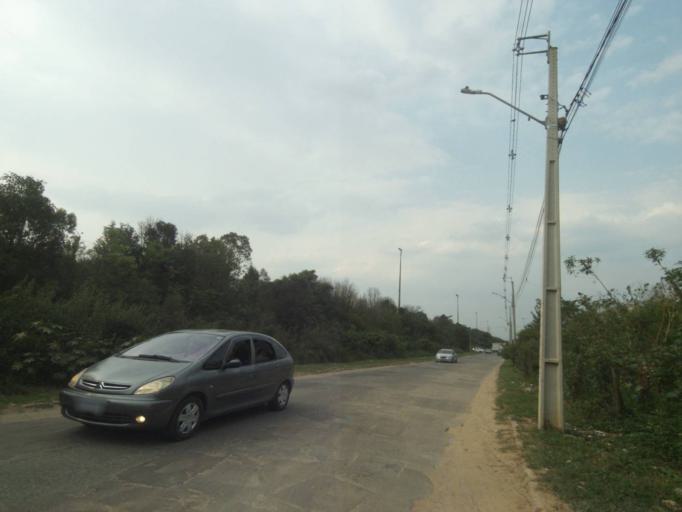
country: BR
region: Parana
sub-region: Sao Jose Dos Pinhais
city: Sao Jose dos Pinhais
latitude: -25.5307
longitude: -49.2299
